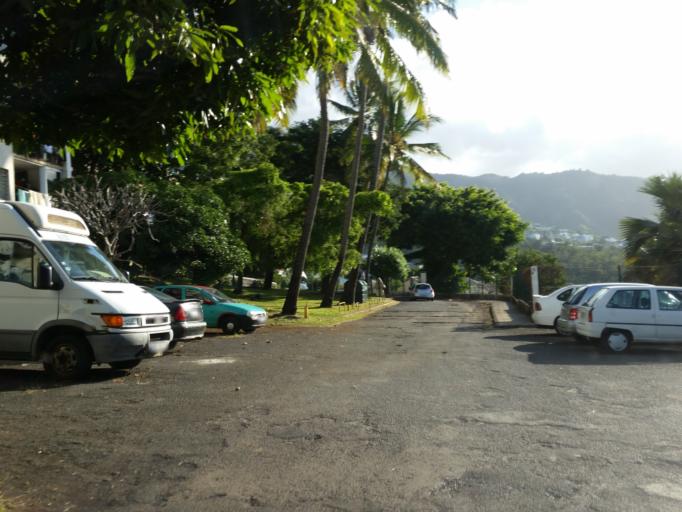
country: RE
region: Reunion
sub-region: Reunion
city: Saint-Denis
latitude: -20.8988
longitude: 55.4622
